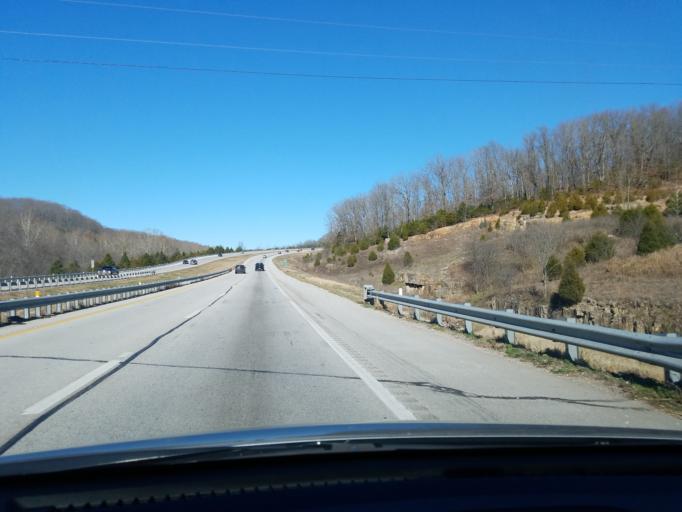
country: US
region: Missouri
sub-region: Christian County
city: Ozark
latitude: 36.9087
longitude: -93.2430
